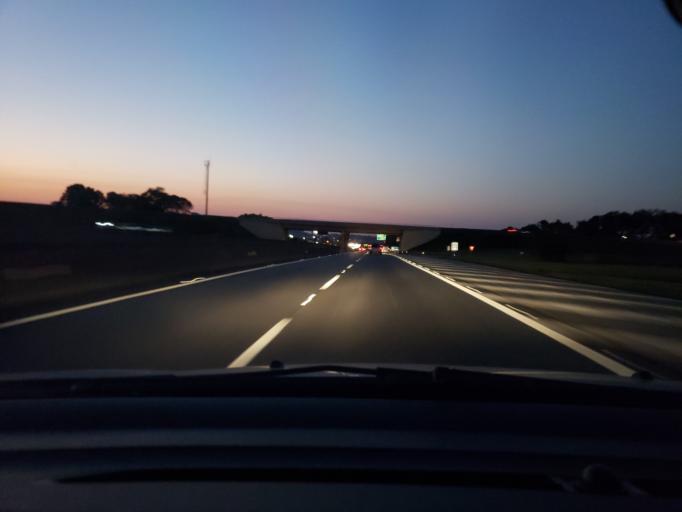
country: BR
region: Sao Paulo
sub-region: Campinas
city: Campinas
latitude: -22.8980
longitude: -47.1101
